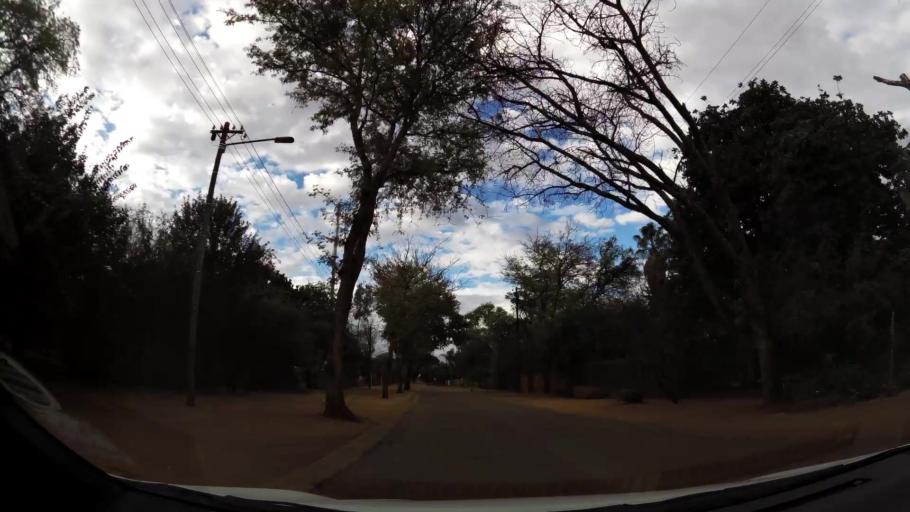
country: ZA
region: Limpopo
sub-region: Waterberg District Municipality
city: Modimolle
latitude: -24.5115
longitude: 28.7143
